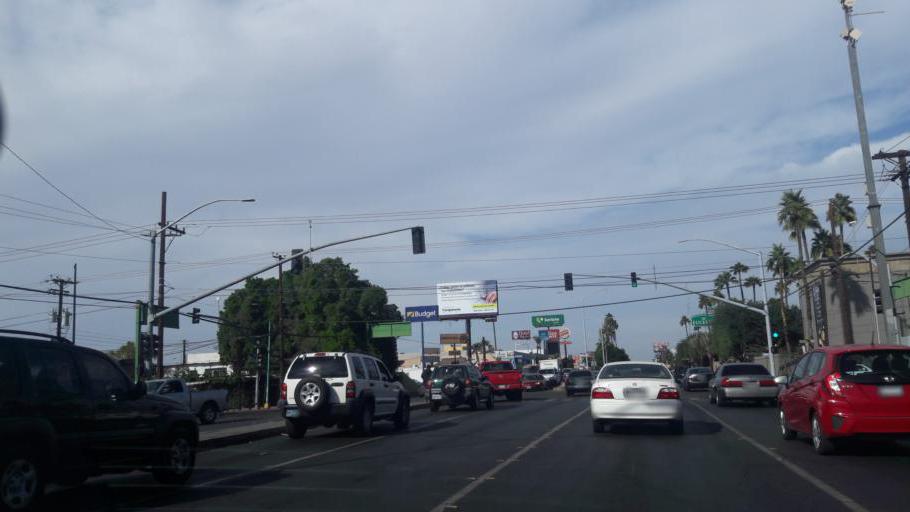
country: MX
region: Baja California
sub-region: Mexicali
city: Mexicali
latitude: 32.6368
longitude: -115.4482
